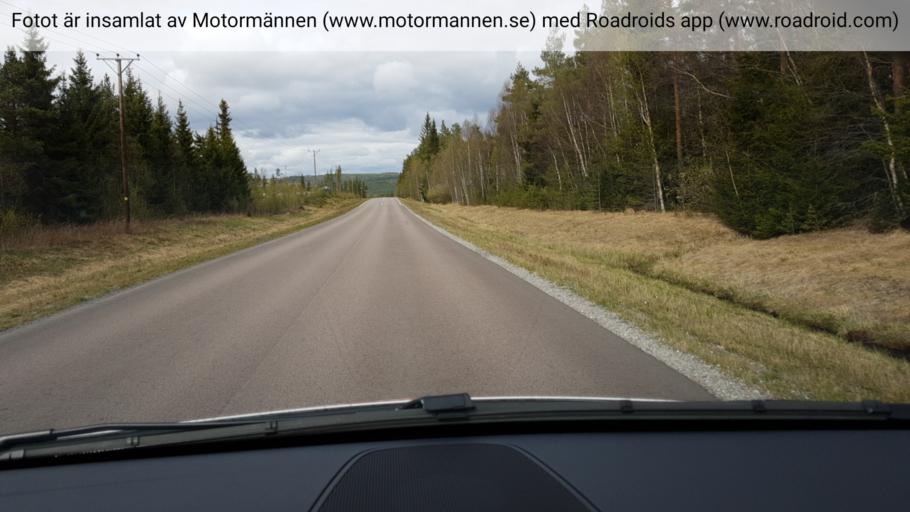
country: SE
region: Jaemtland
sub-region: Ragunda Kommun
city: Hammarstrand
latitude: 63.1952
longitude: 15.9416
